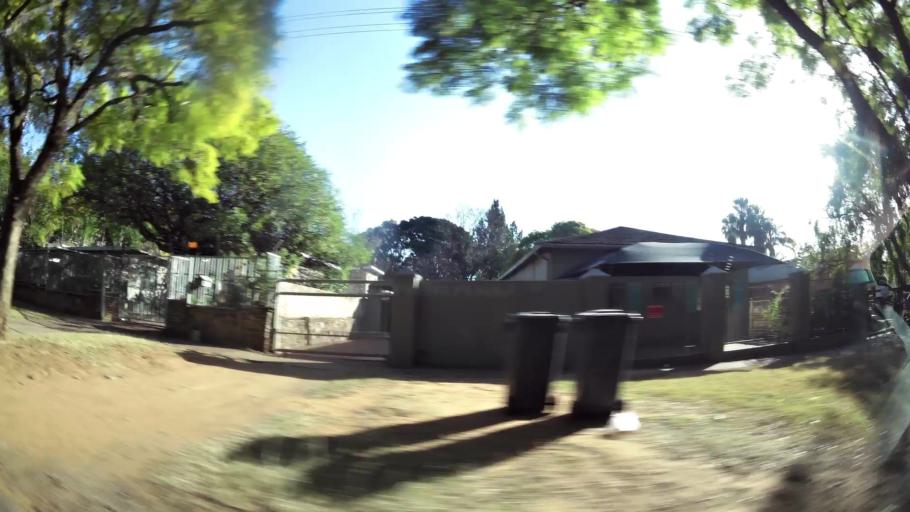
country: ZA
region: Gauteng
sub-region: City of Tshwane Metropolitan Municipality
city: Pretoria
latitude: -25.7266
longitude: 28.2132
